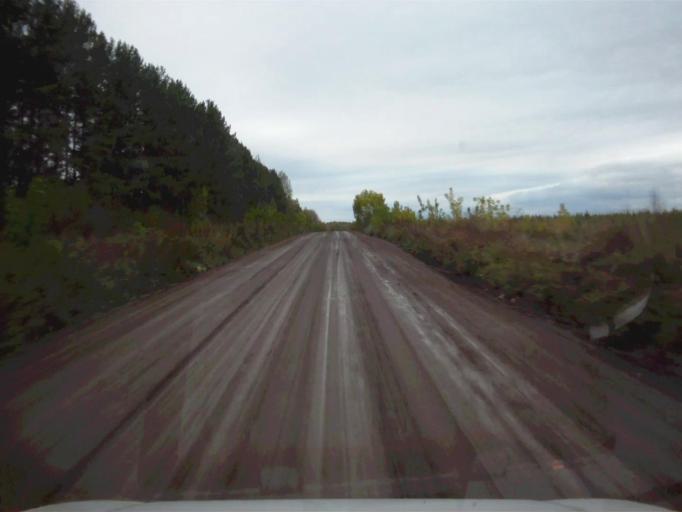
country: RU
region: Sverdlovsk
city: Mikhaylovsk
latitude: 56.1612
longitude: 59.2467
